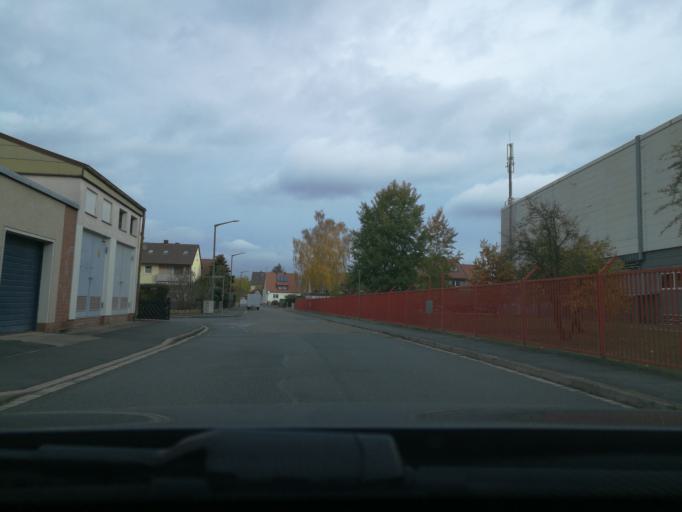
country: DE
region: Bavaria
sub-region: Regierungsbezirk Mittelfranken
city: Furth
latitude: 49.5131
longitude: 10.9836
